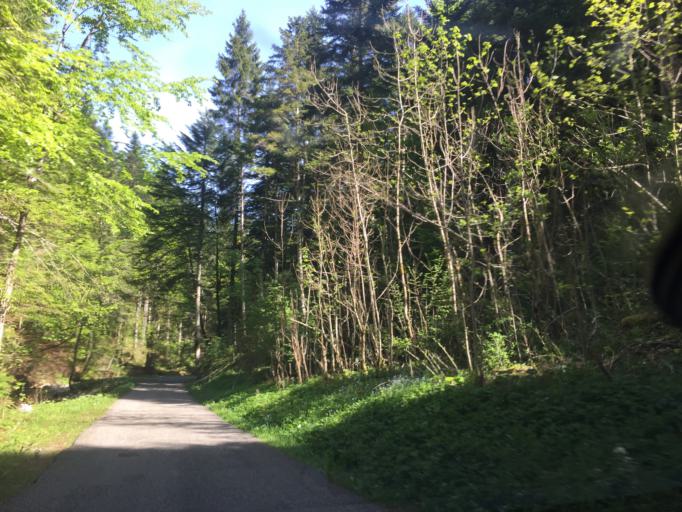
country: FR
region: Rhone-Alpes
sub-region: Departement de l'Isere
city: Le Sappey-en-Chartreuse
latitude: 45.3041
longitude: 5.8109
